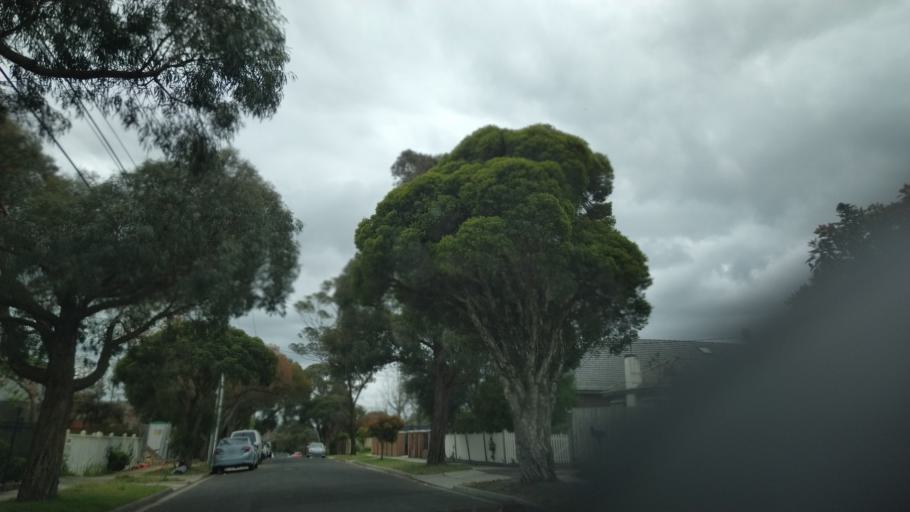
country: AU
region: Victoria
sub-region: Glen Eira
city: Murrumbeena
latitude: -37.8832
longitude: 145.0765
